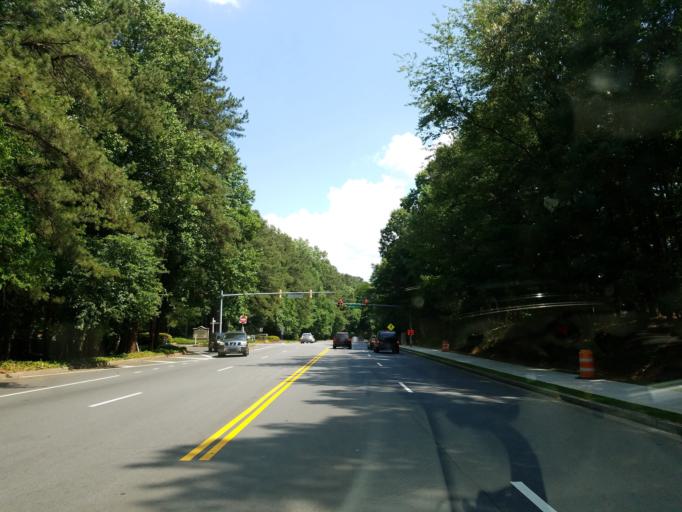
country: US
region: Georgia
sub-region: Cobb County
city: Smyrna
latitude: 33.8957
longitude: -84.4924
